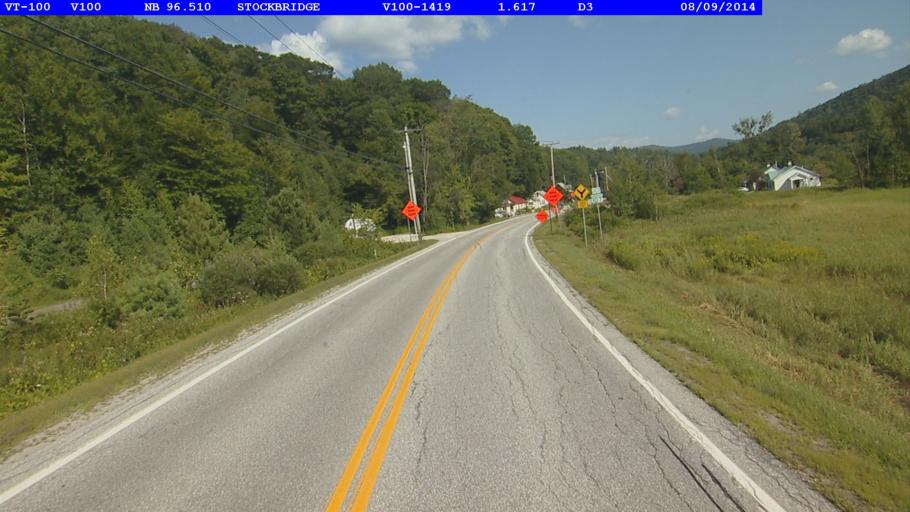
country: US
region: Vermont
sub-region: Orange County
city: Randolph
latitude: 43.7764
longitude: -72.7674
